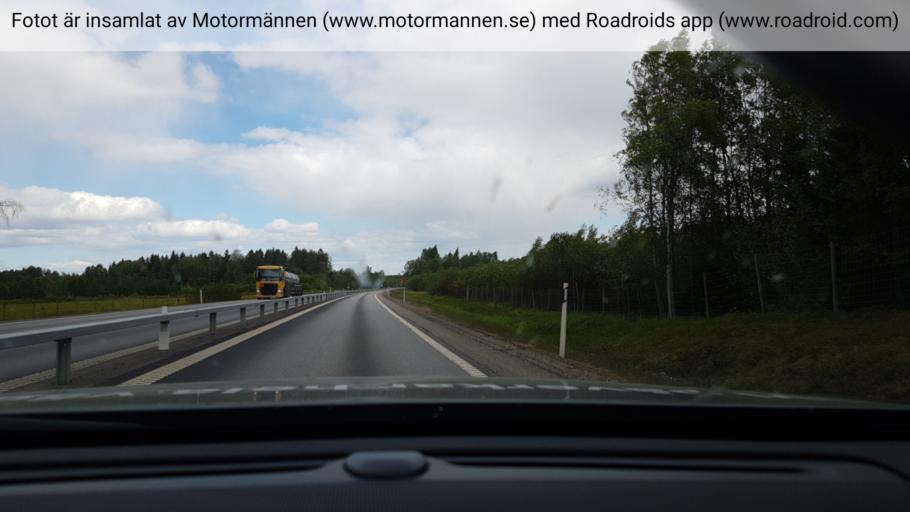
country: SE
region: Vaesterbotten
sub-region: Umea Kommun
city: Hoernefors
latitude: 63.6360
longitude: 19.9000
